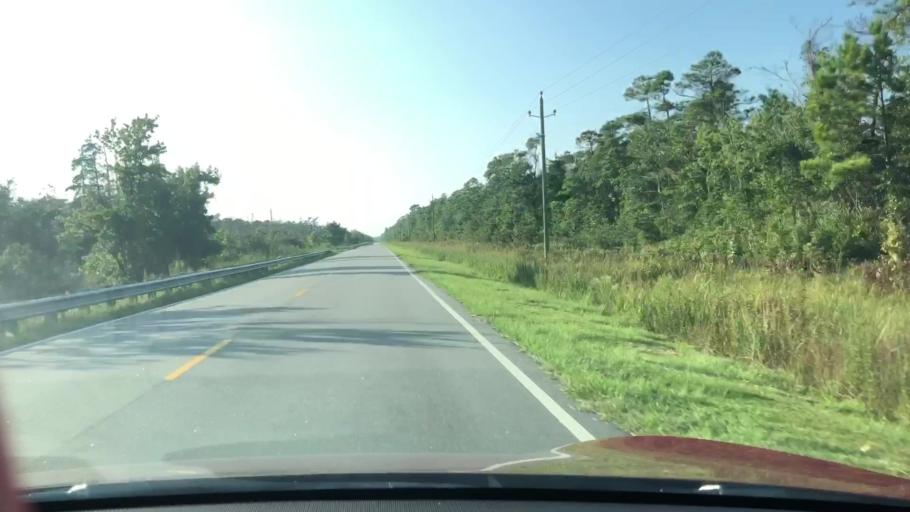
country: US
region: North Carolina
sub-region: Dare County
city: Manteo
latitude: 35.8104
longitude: -75.7907
